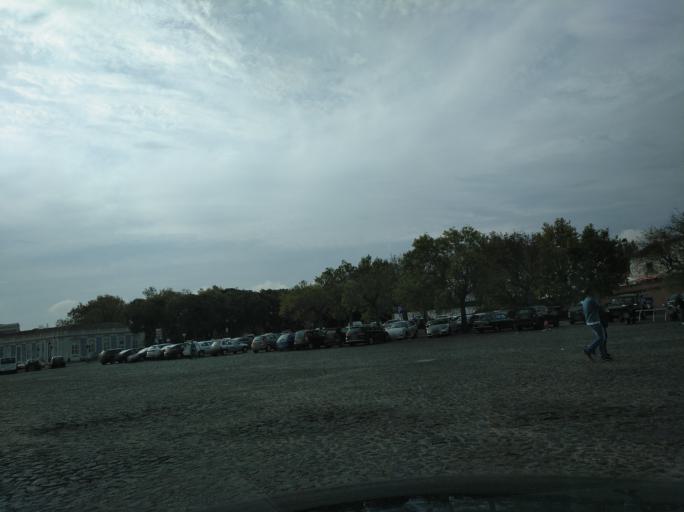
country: PT
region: Lisbon
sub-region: Sintra
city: Queluz
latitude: 38.7514
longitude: -9.2572
